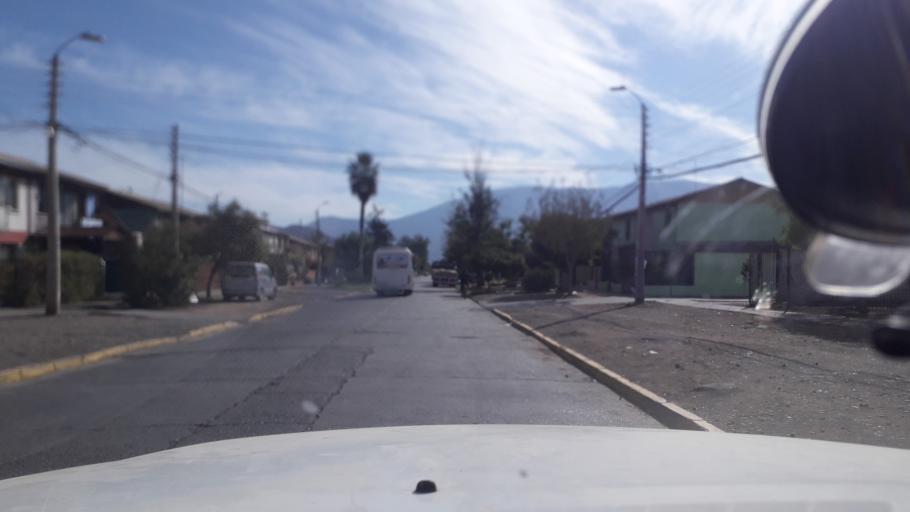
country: CL
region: Valparaiso
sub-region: Provincia de San Felipe
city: San Felipe
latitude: -32.7512
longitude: -70.7158
